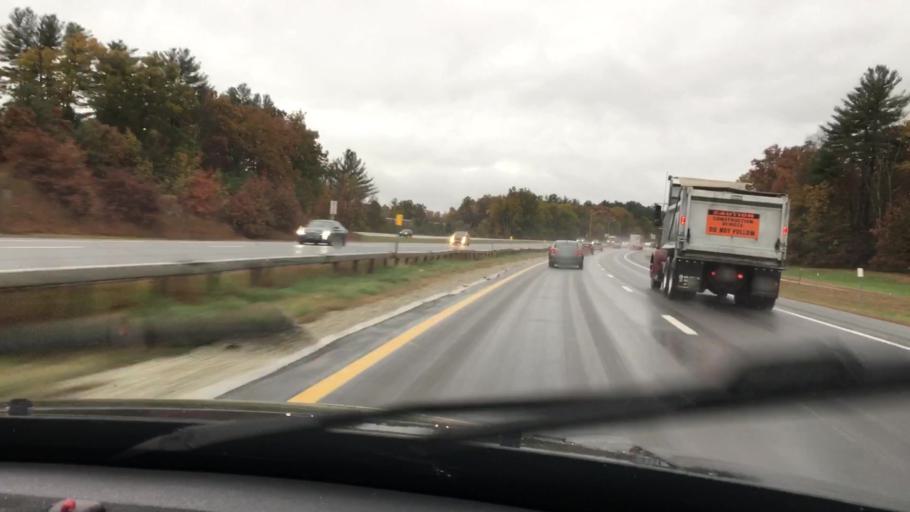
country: US
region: New Hampshire
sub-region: Hillsborough County
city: East Merrimack
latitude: 42.8844
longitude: -71.4801
